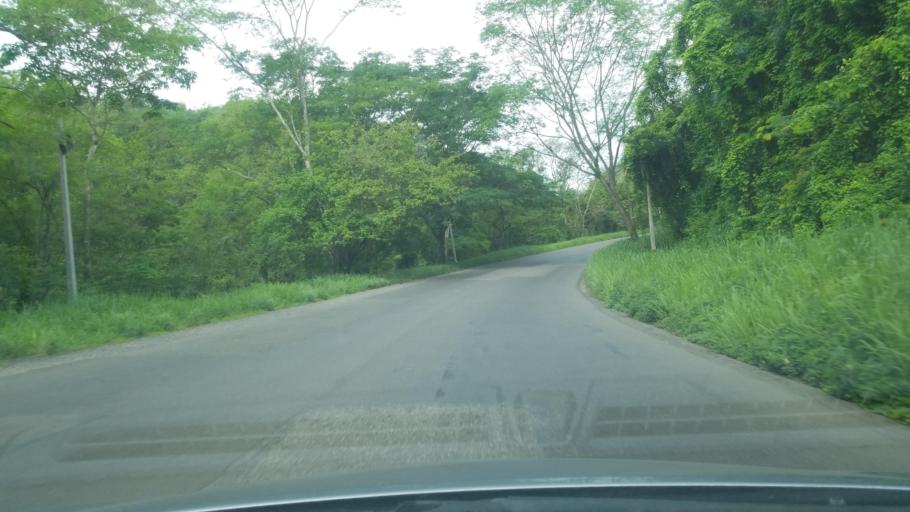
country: HN
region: Santa Barbara
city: Camalote
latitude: 15.3258
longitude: -88.3055
